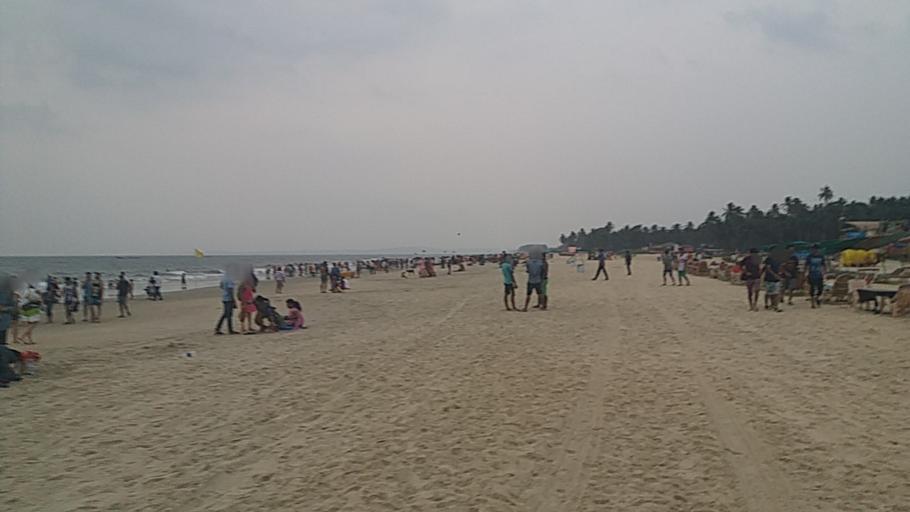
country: IN
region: Goa
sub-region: South Goa
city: Colva
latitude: 15.2746
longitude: 73.9136
